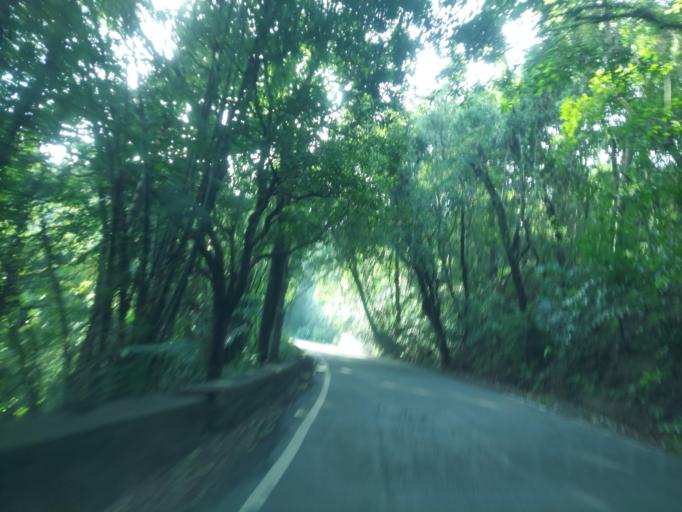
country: IN
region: Maharashtra
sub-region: Sindhudurg
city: Savantvadi
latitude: 15.9352
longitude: 73.9415
